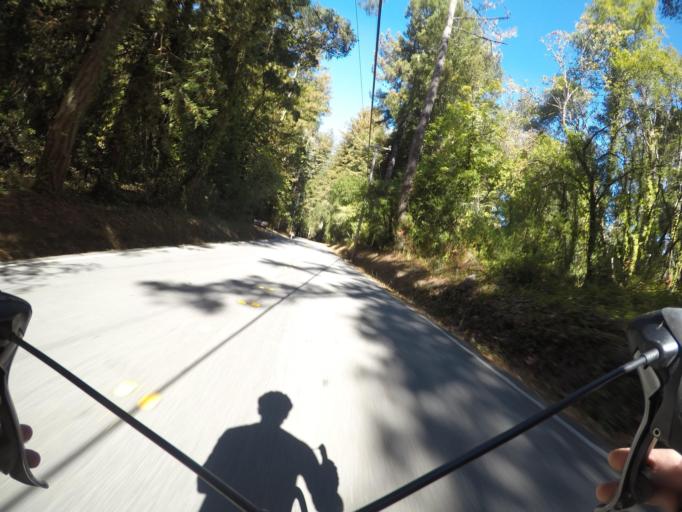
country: US
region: California
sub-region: San Mateo County
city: Portola Valley
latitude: 37.2970
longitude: -122.2648
